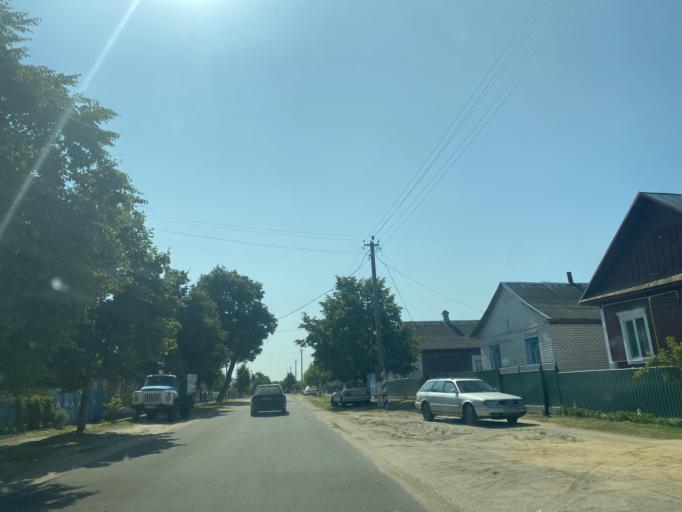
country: BY
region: Brest
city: Ivanava
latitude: 52.3149
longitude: 25.6130
